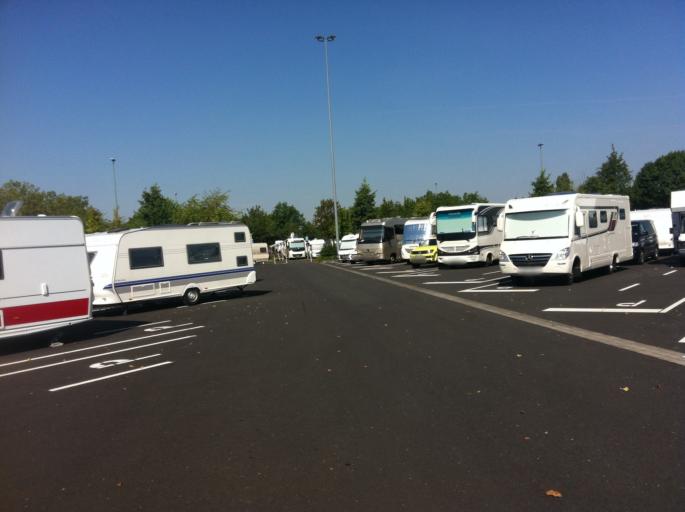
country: DE
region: North Rhine-Westphalia
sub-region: Regierungsbezirk Dusseldorf
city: Meerbusch
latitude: 51.2684
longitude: 6.7193
